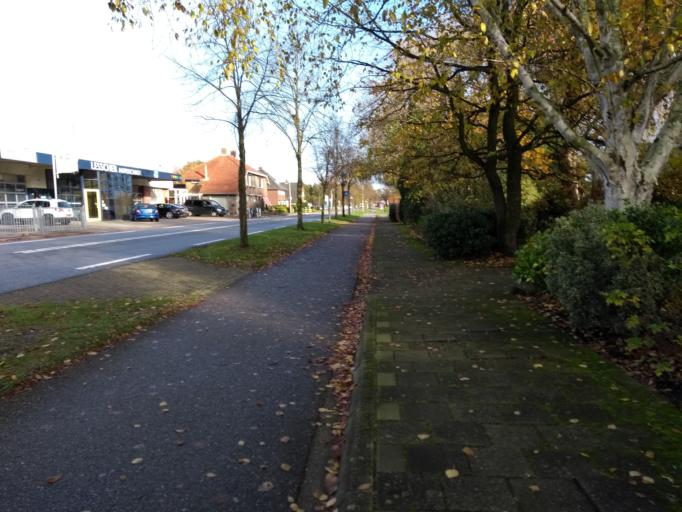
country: NL
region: Overijssel
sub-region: Gemeente Almelo
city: Almelo
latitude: 52.3799
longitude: 6.7072
